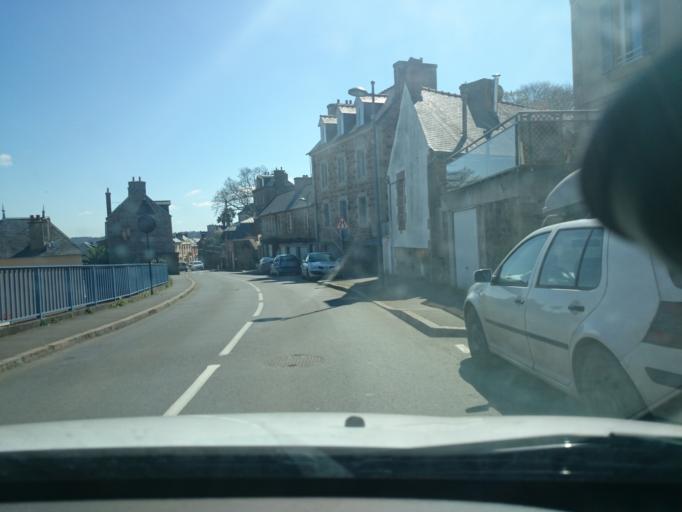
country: FR
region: Brittany
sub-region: Departement des Cotes-d'Armor
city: Perros-Guirec
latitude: 48.8132
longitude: -3.4417
